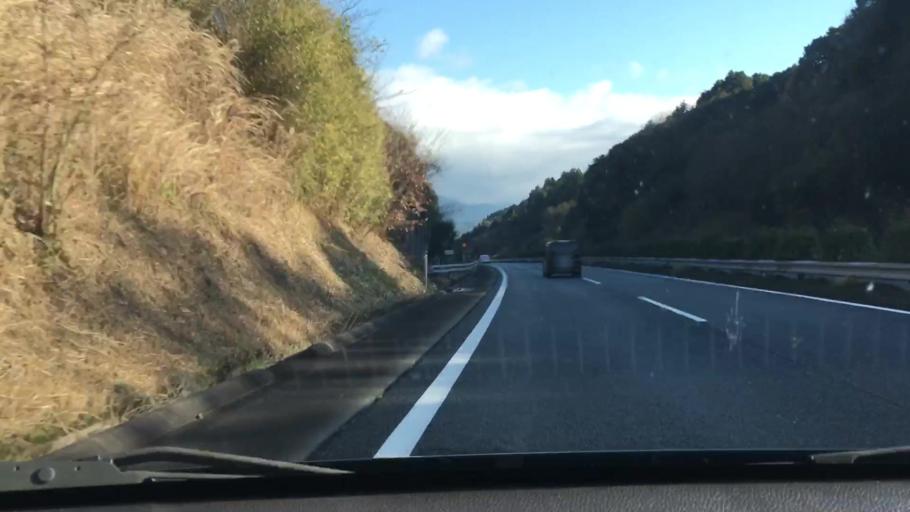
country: JP
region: Kumamoto
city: Hitoyoshi
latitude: 32.1840
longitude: 130.7792
